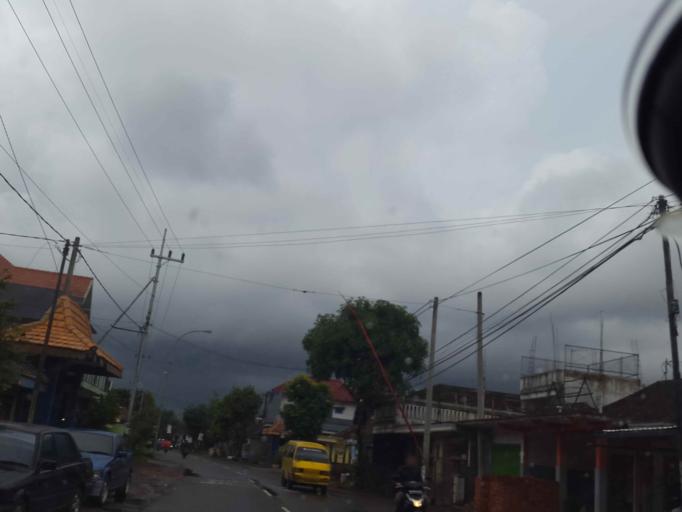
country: ID
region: East Java
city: Batu
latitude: -7.8639
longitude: 112.5548
